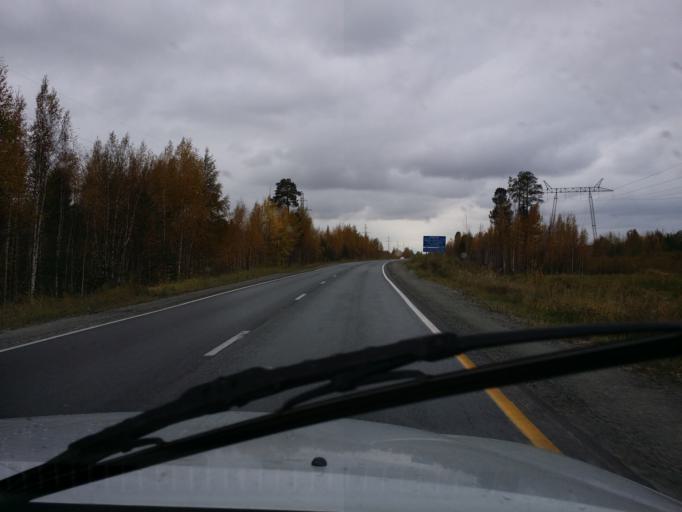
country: RU
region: Khanty-Mansiyskiy Avtonomnyy Okrug
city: Megion
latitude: 61.1013
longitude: 75.9655
